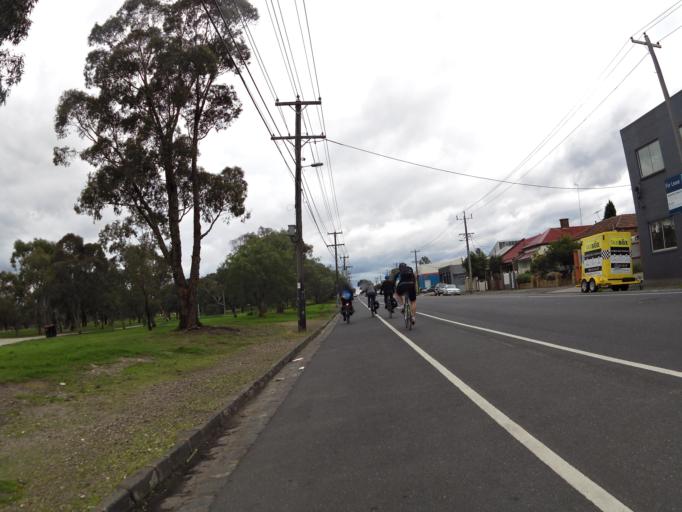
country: AU
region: Victoria
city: Brunswick West
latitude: -37.7677
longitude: 144.9525
